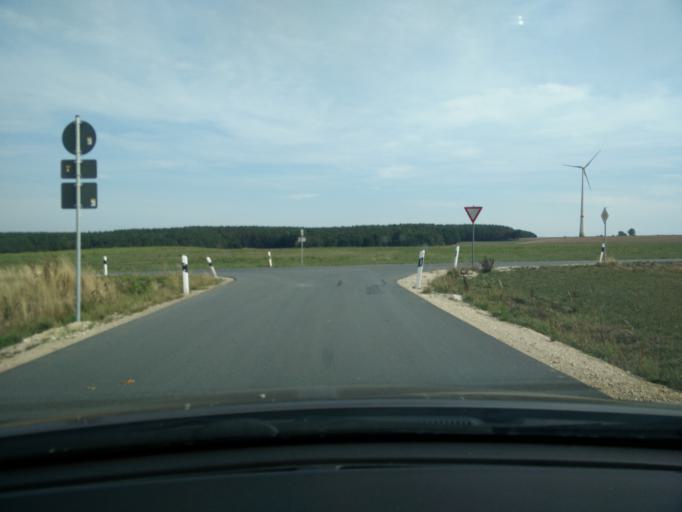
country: DE
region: Bavaria
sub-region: Regierungsbezirk Mittelfranken
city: Hagenbuchach
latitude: 49.5518
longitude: 10.7980
